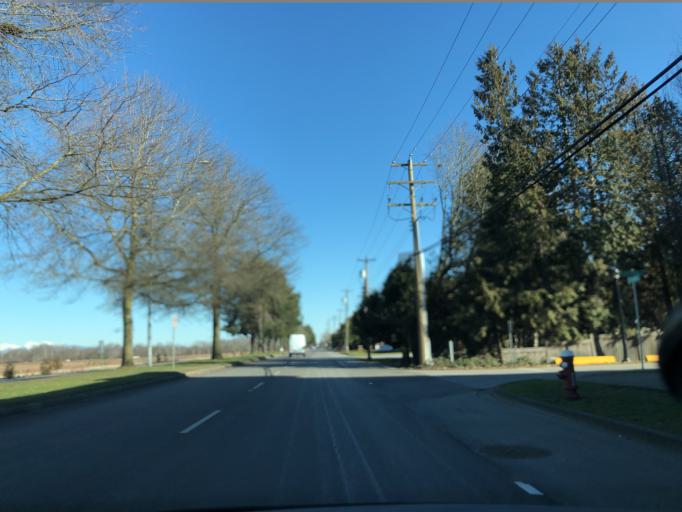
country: CA
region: British Columbia
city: Richmond
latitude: 49.1701
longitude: -123.1230
